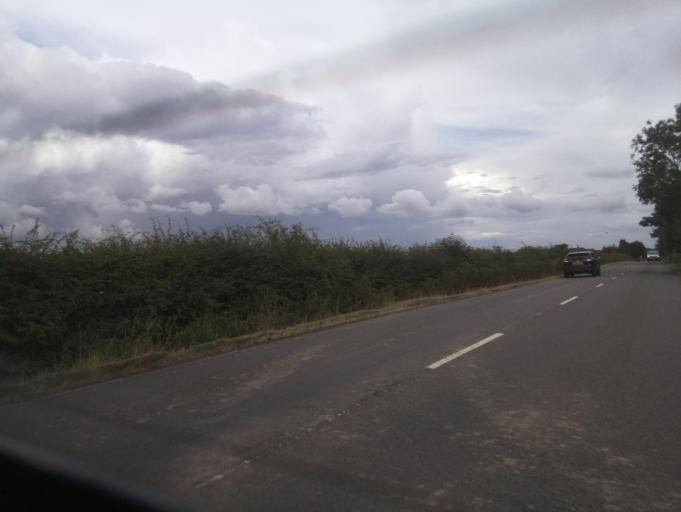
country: GB
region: England
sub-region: Staffordshire
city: Eccleshall
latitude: 52.8300
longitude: -2.2830
